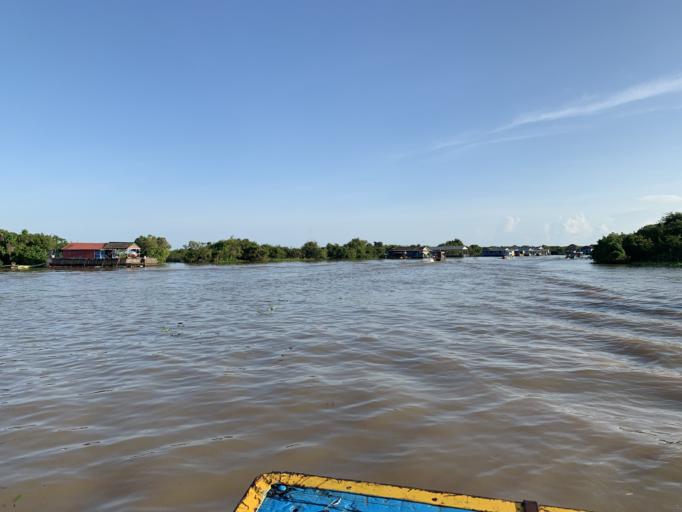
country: KH
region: Siem Reap
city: Siem Reap
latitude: 13.2476
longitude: 103.8231
